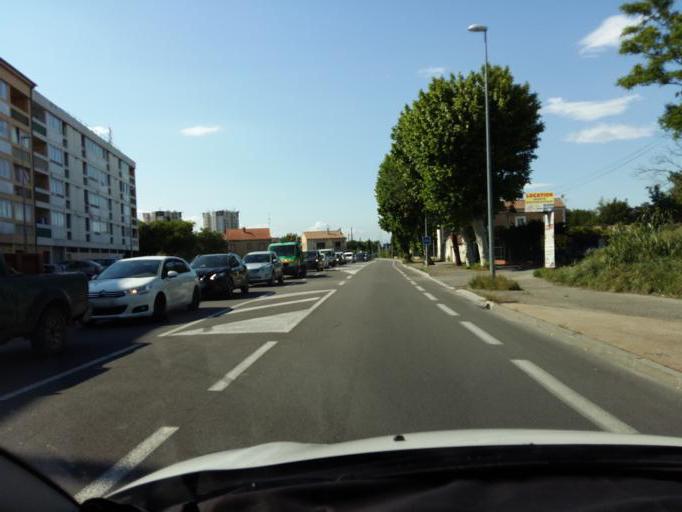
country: FR
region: Provence-Alpes-Cote d'Azur
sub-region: Departement du Vaucluse
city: Cavaillon
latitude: 43.8416
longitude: 5.0463
